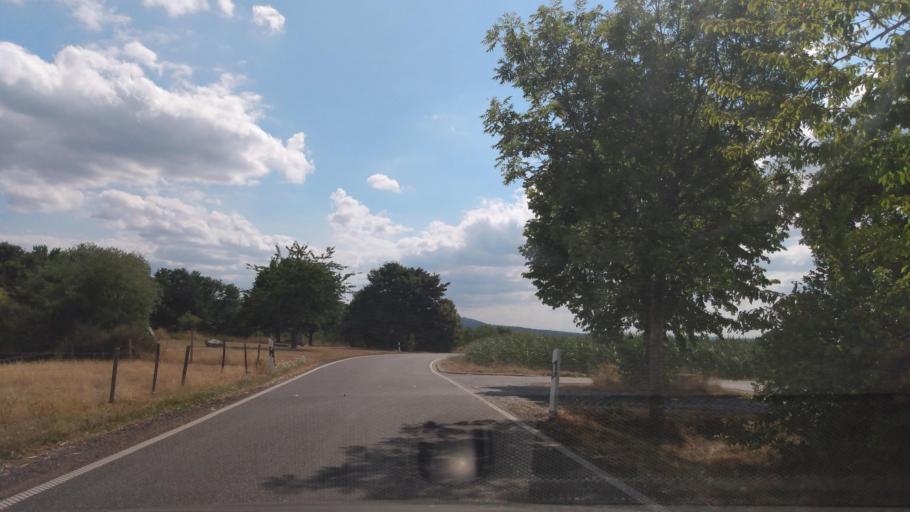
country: DE
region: Rheinland-Pfalz
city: Morbach
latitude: 49.7787
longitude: 7.0949
